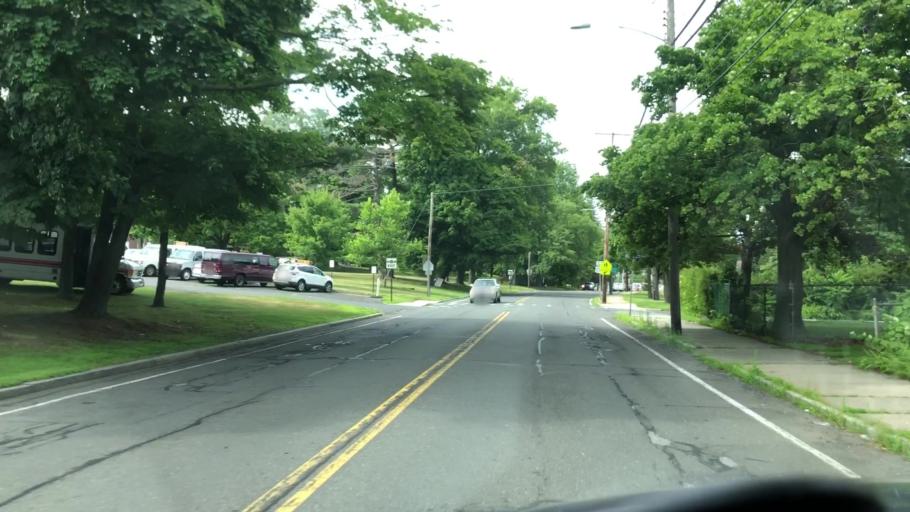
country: US
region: Massachusetts
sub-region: Hampden County
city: Holyoke
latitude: 42.1966
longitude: -72.6307
